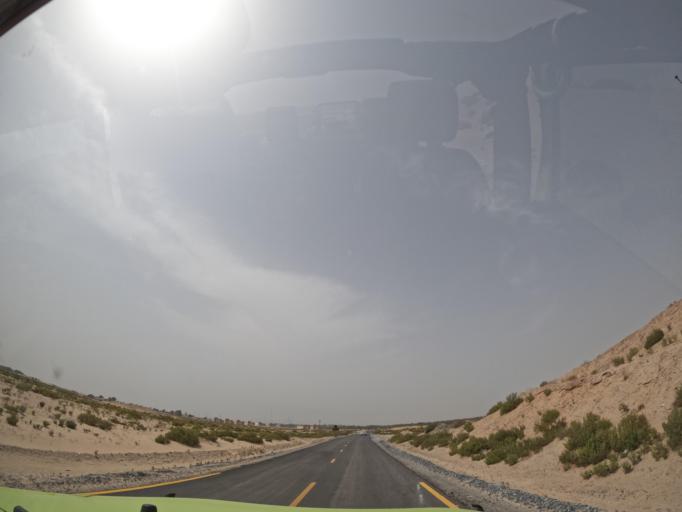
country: AE
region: Dubai
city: Dubai
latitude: 25.1268
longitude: 55.3425
